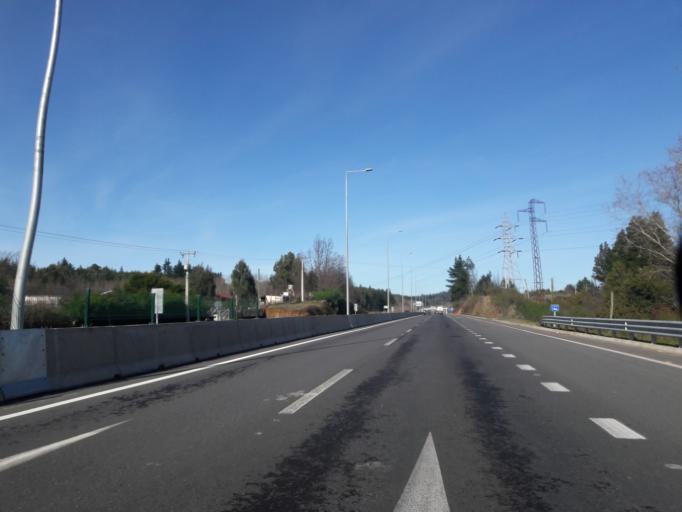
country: CL
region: Biobio
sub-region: Provincia de Concepcion
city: Chiguayante
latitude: -36.9101
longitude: -72.7782
